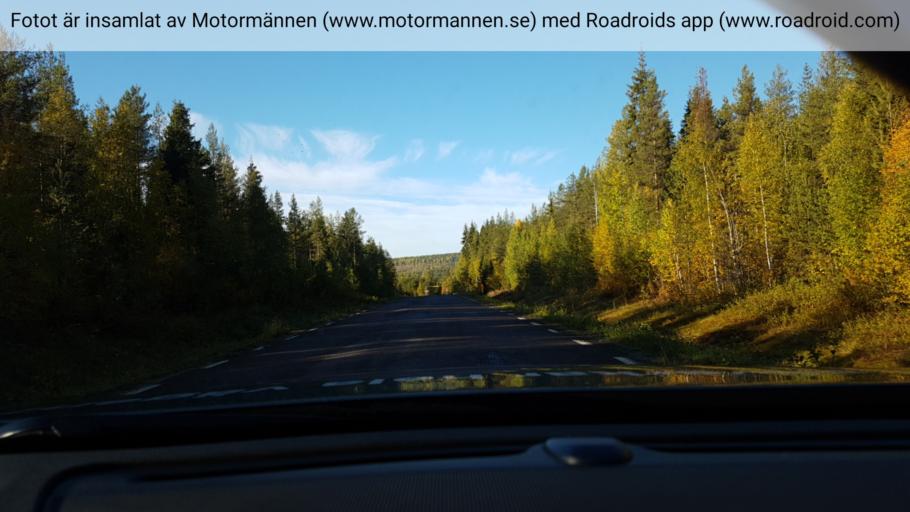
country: SE
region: Norrbotten
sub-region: Bodens Kommun
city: Boden
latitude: 66.0599
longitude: 21.4229
